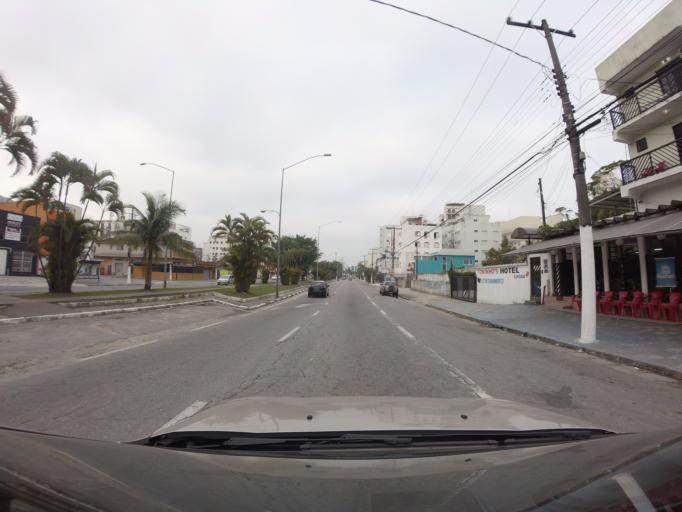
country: BR
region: Sao Paulo
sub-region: Guaruja
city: Guaruja
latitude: -23.9849
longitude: -46.2402
